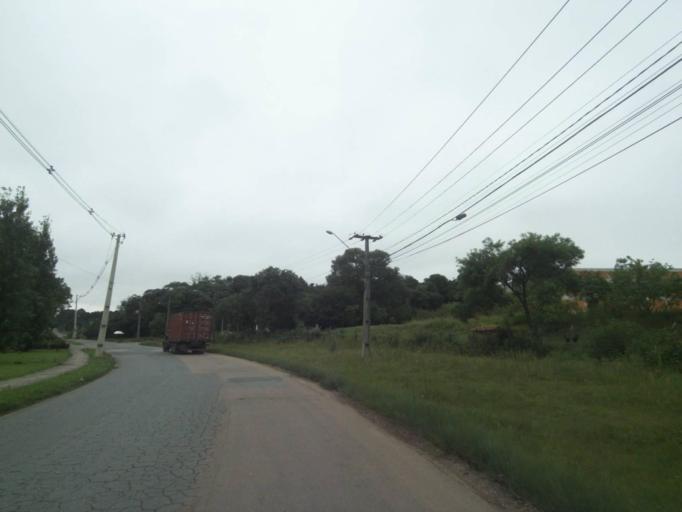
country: BR
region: Parana
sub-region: Araucaria
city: Araucaria
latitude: -25.5436
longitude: -49.3230
